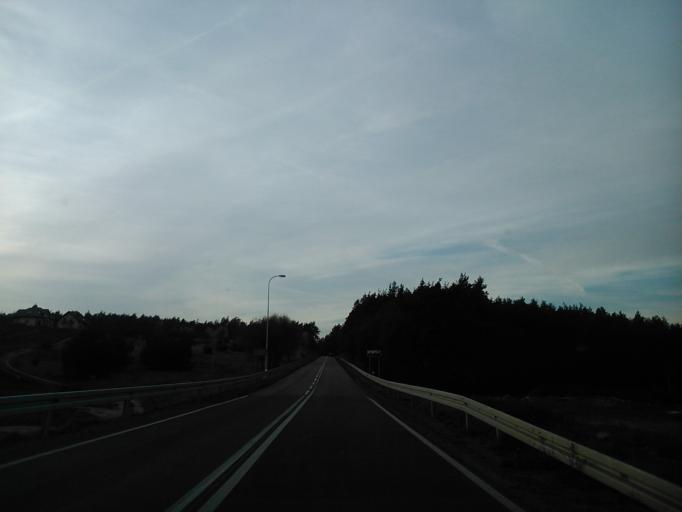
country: PL
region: Warmian-Masurian Voivodeship
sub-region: Powiat dzialdowski
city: Lidzbark
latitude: 53.2690
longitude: 19.8159
